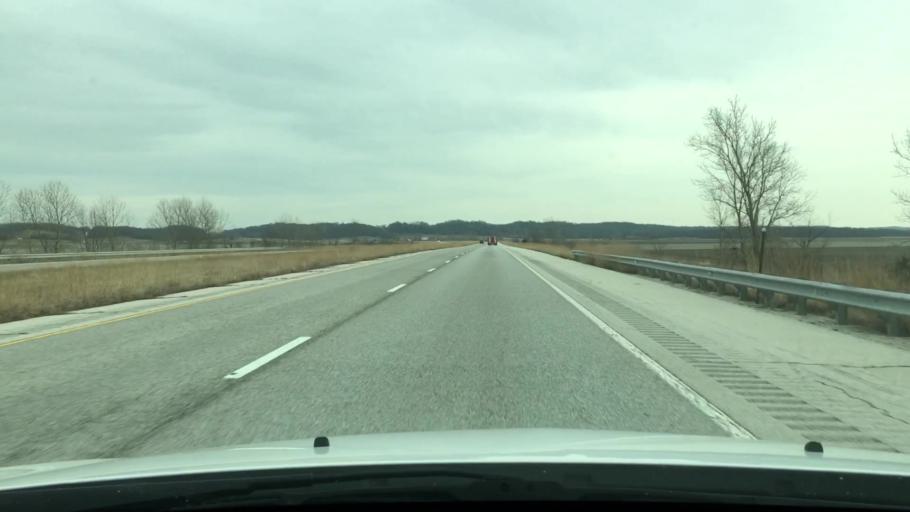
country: US
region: Illinois
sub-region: Pike County
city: Griggsville
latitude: 39.6883
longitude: -90.5976
